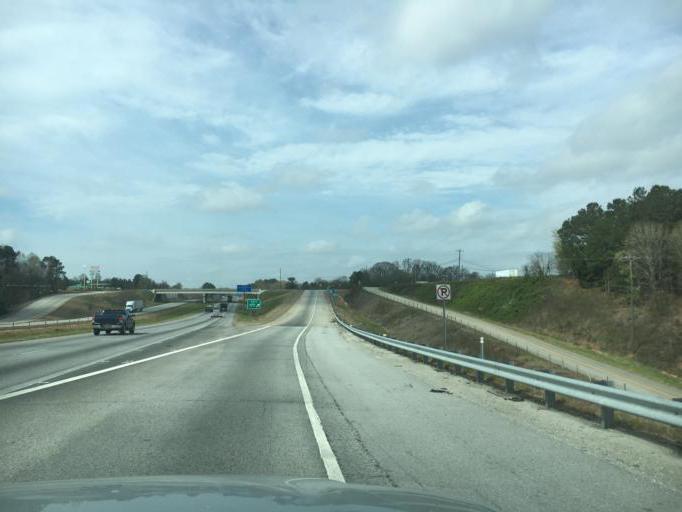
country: US
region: Georgia
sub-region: Franklin County
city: Gumlog
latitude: 34.4754
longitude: -83.0542
